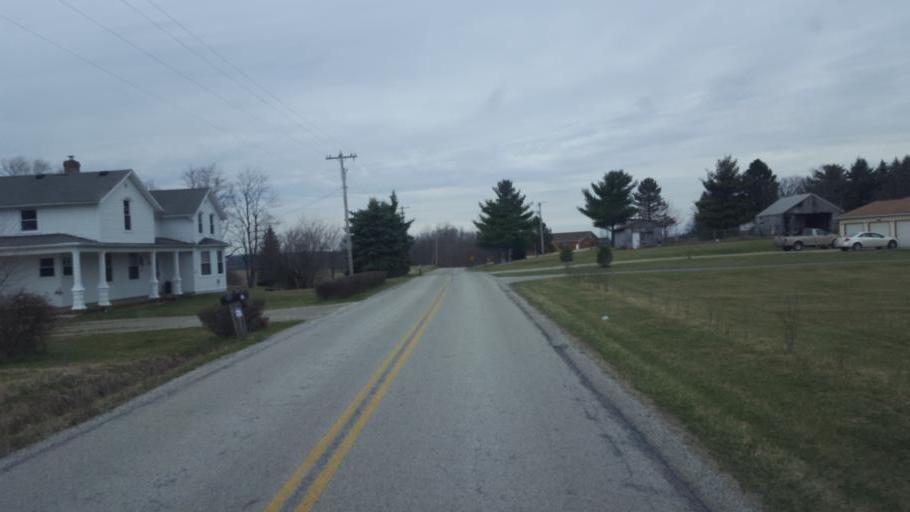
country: US
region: Ohio
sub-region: Richland County
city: Mansfield
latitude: 40.7085
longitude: -82.4791
